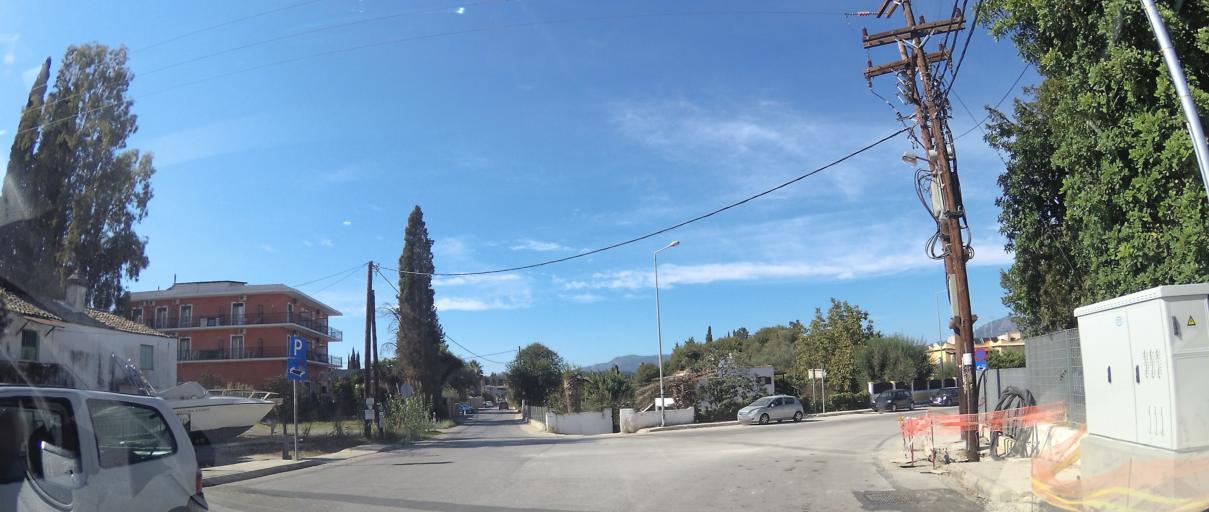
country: GR
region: Ionian Islands
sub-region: Nomos Kerkyras
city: Kontokali
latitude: 39.6435
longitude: 19.8492
